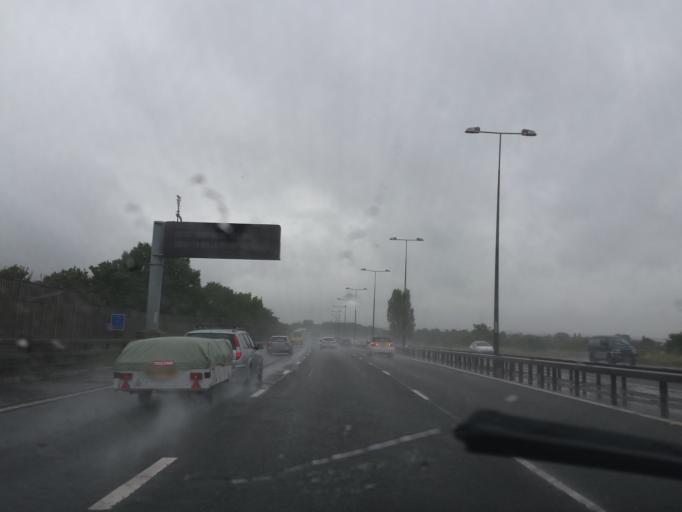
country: GB
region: England
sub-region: Derbyshire
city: Long Eaton
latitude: 52.9046
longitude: -1.2998
